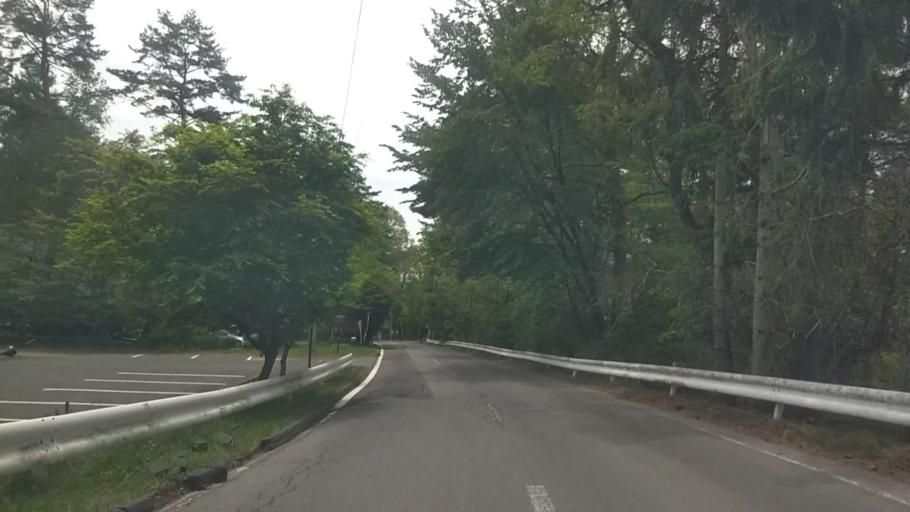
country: JP
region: Nagano
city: Chino
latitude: 36.0366
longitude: 138.2674
